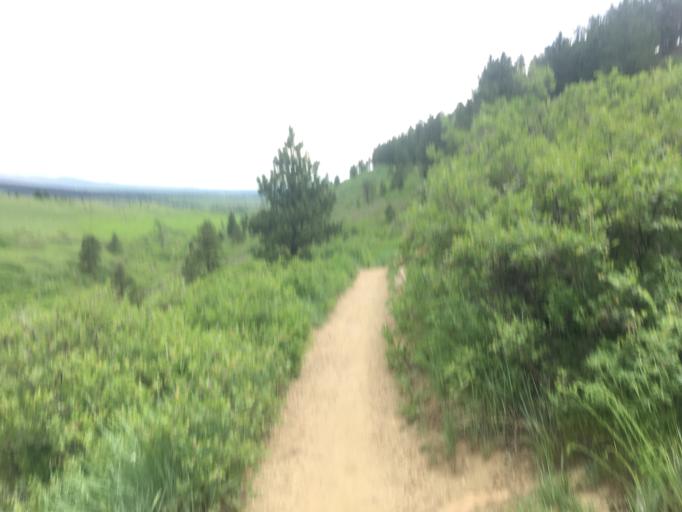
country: US
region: Colorado
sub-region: Boulder County
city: Superior
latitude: 39.9171
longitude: -105.2600
